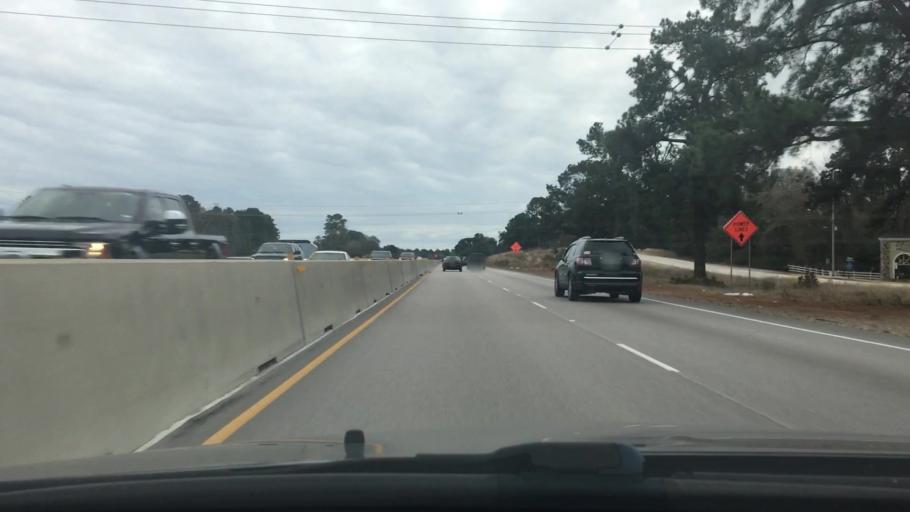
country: US
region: Texas
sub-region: Walker County
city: Huntsville
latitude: 30.6684
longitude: -95.5155
